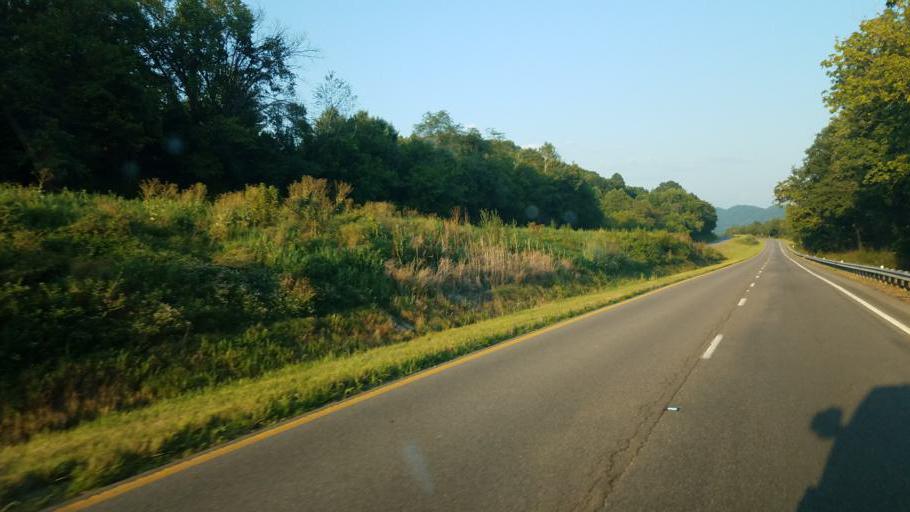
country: US
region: Virginia
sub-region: Scott County
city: Gate City
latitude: 36.6358
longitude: -82.6467
